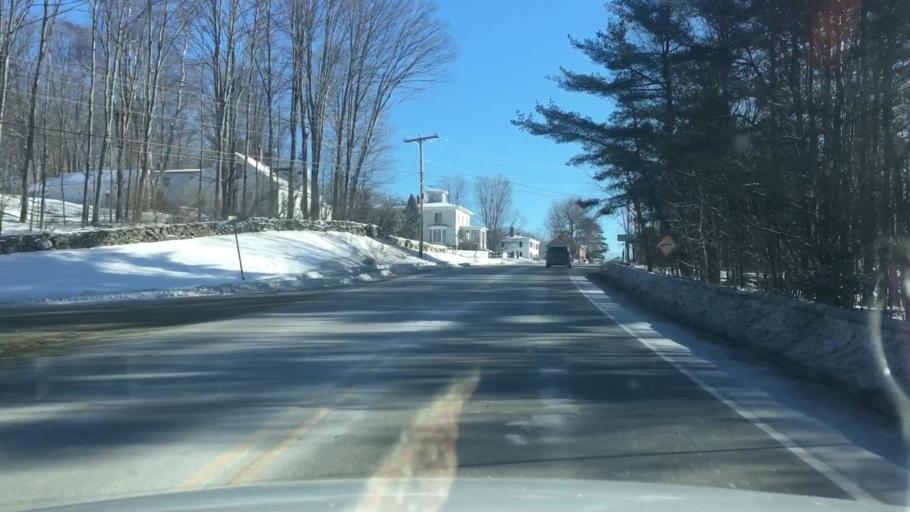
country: US
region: Maine
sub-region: Kennebec County
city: Readfield
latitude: 44.3880
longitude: -69.9702
